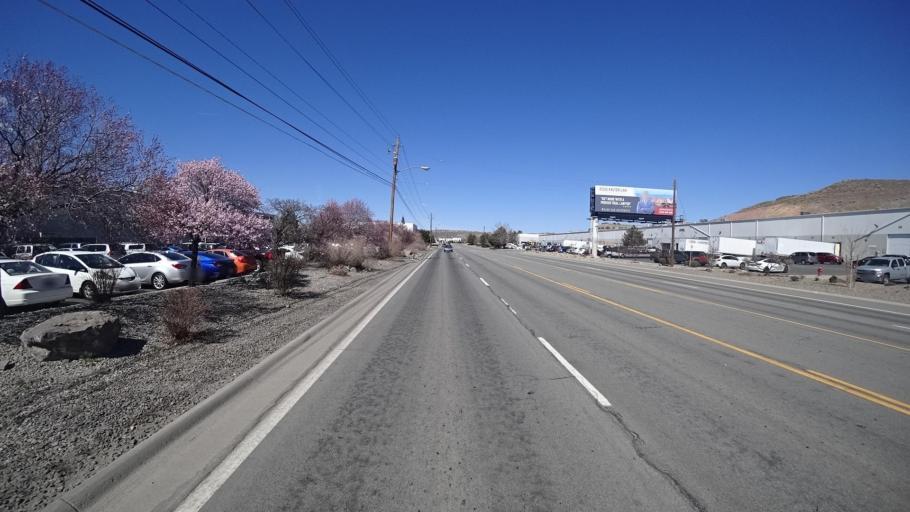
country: US
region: Nevada
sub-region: Washoe County
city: Sparks
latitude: 39.5338
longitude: -119.7039
